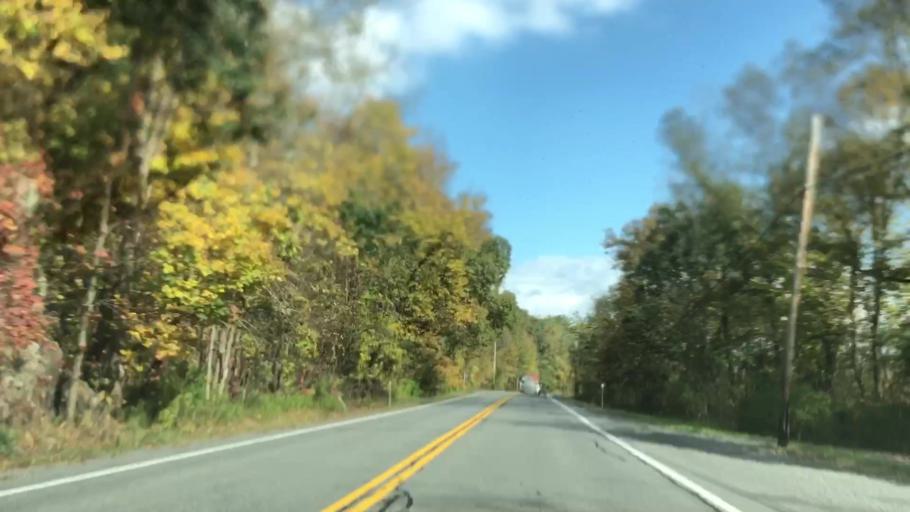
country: US
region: New York
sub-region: Warren County
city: Queensbury
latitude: 43.4244
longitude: -73.4814
